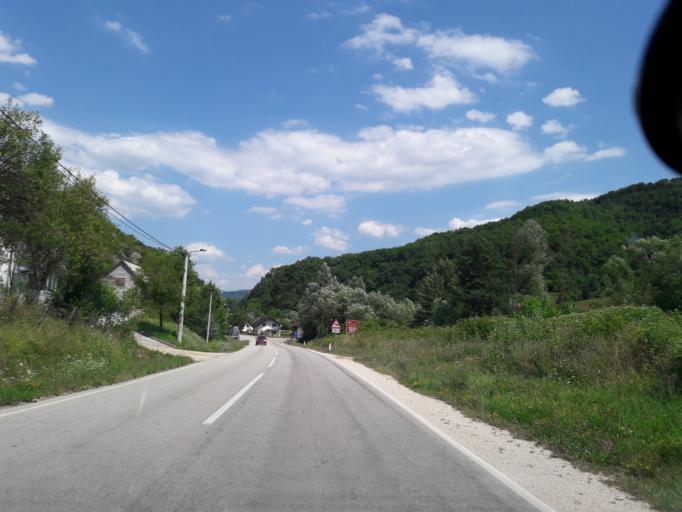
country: BA
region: Republika Srpska
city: Mrkonjic Grad
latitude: 44.4221
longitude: 17.1185
